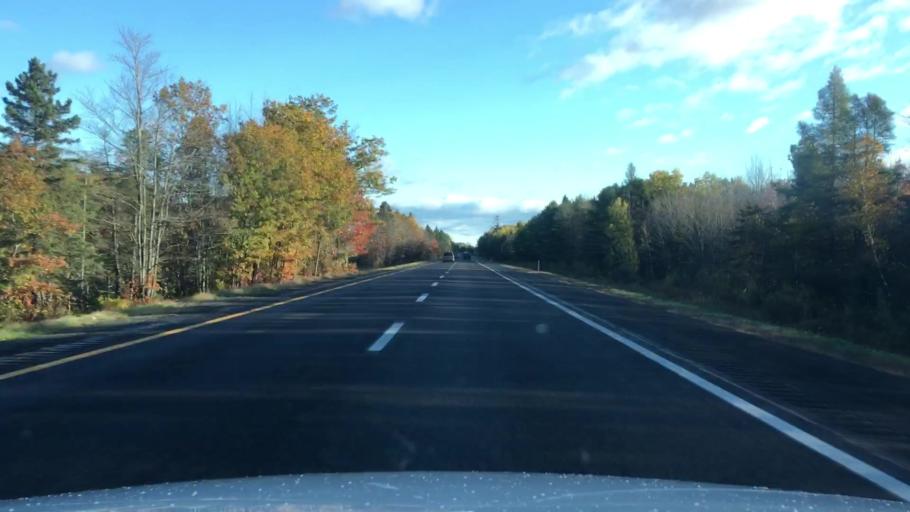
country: US
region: Maine
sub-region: Penobscot County
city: Veazie
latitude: 44.8488
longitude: -68.7280
